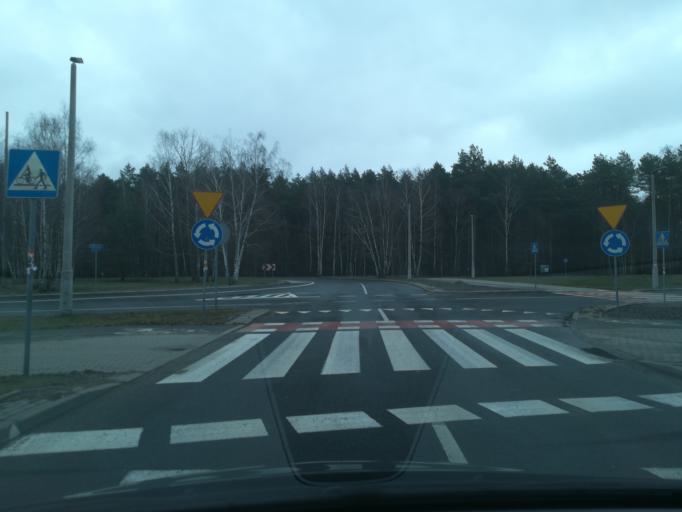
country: PL
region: Kujawsko-Pomorskie
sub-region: Powiat torunski
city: Lubicz Dolny
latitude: 53.0261
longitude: 18.7032
